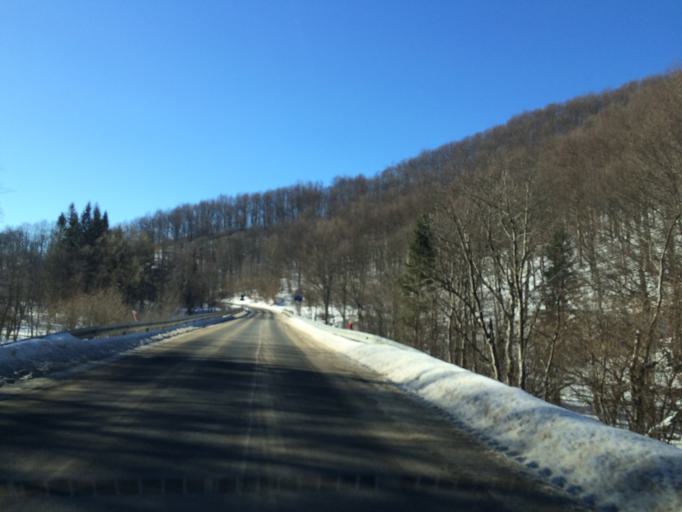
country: PL
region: Subcarpathian Voivodeship
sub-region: Powiat bieszczadzki
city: Lutowiska
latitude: 49.1452
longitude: 22.6693
